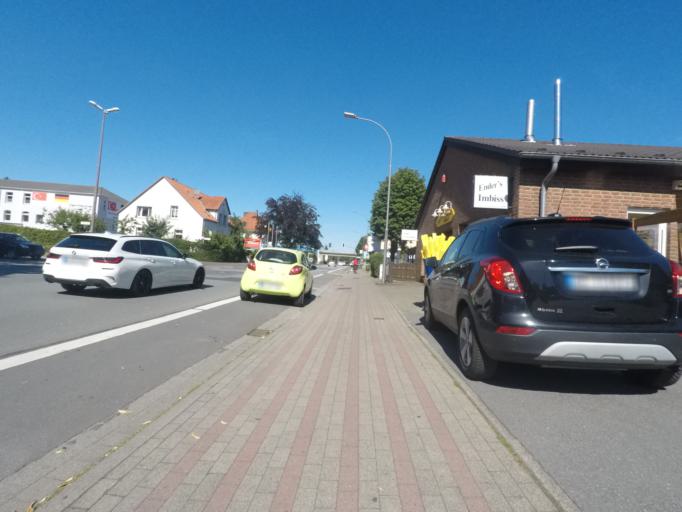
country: DE
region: North Rhine-Westphalia
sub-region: Regierungsbezirk Detmold
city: Herford
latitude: 52.1090
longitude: 8.6569
